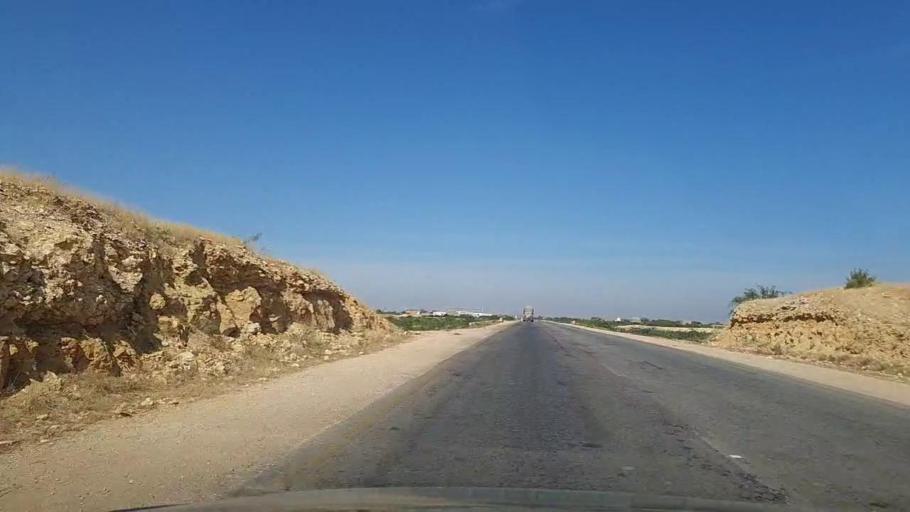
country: PK
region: Sindh
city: Kotri
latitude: 25.2107
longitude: 68.2376
